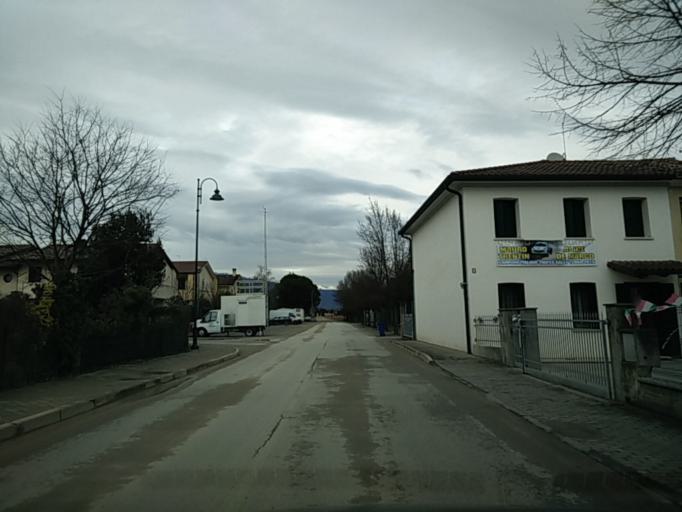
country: IT
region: Veneto
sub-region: Provincia di Treviso
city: Loria Bessica
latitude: 45.7516
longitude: 11.8791
